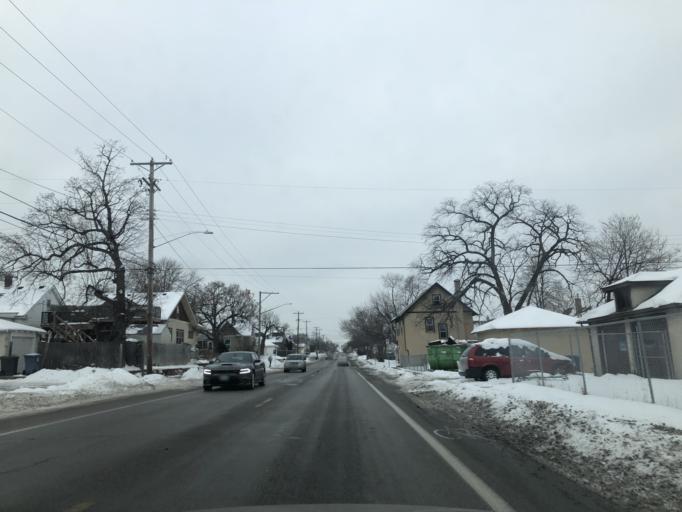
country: US
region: Minnesota
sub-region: Anoka County
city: Columbia Heights
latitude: 45.0240
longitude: -93.2896
